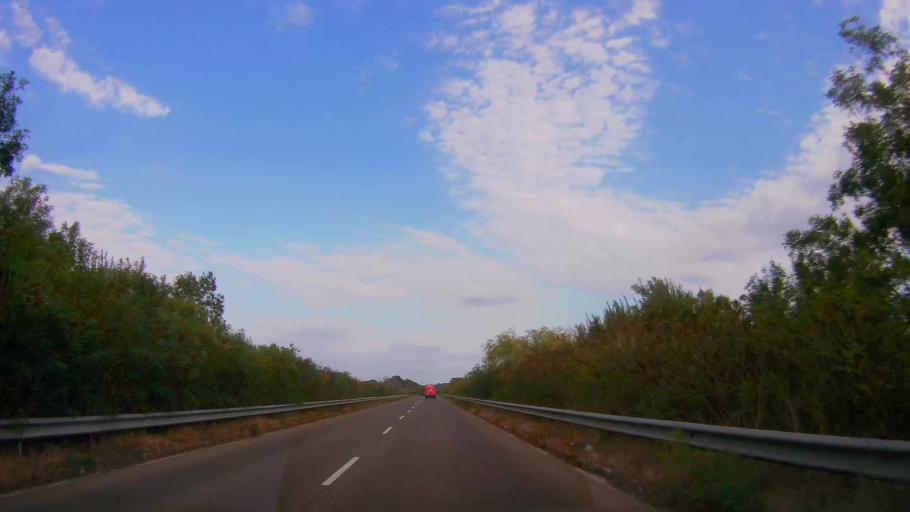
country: BG
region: Burgas
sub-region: Obshtina Sozopol
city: Sozopol
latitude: 42.3542
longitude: 27.7071
